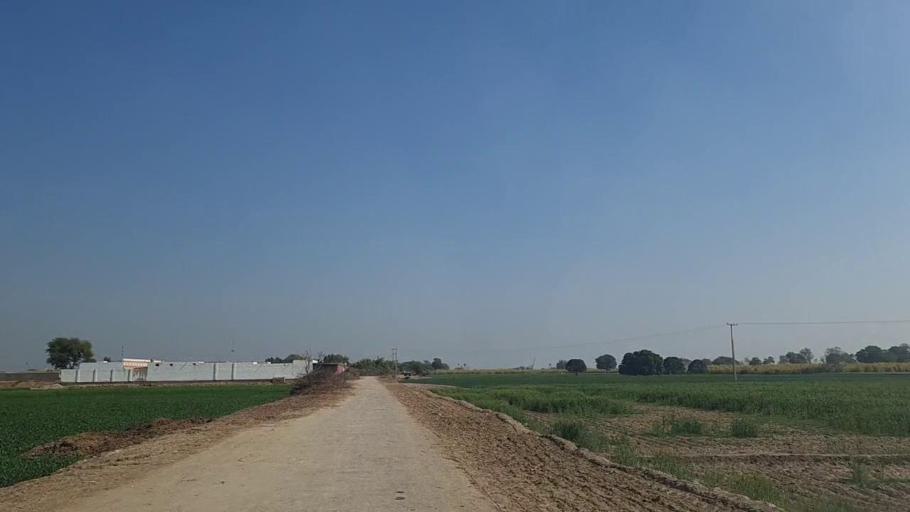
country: PK
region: Sindh
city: Shahpur Chakar
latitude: 26.2026
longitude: 68.5767
